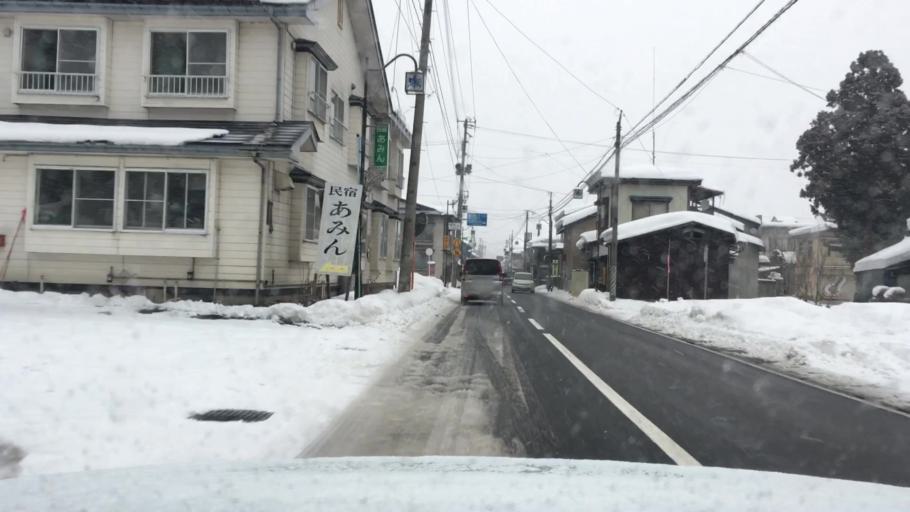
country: JP
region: Iwate
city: Ichinohe
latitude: 40.0966
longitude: 141.0474
